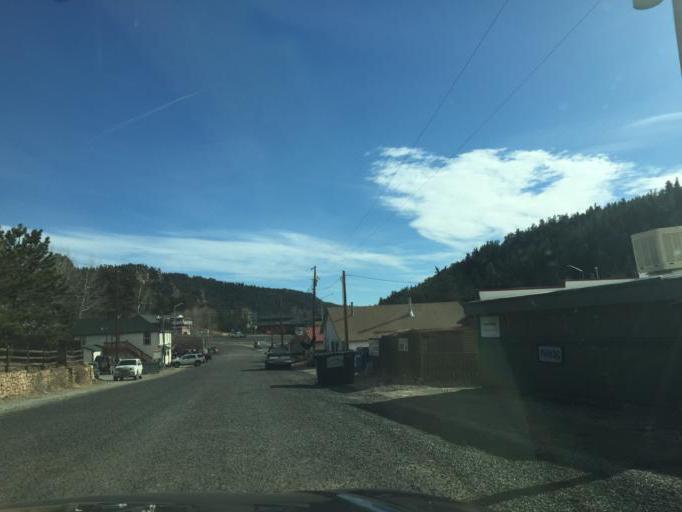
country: US
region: Colorado
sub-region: Jefferson County
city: Evergreen
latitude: 39.4061
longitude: -105.4762
